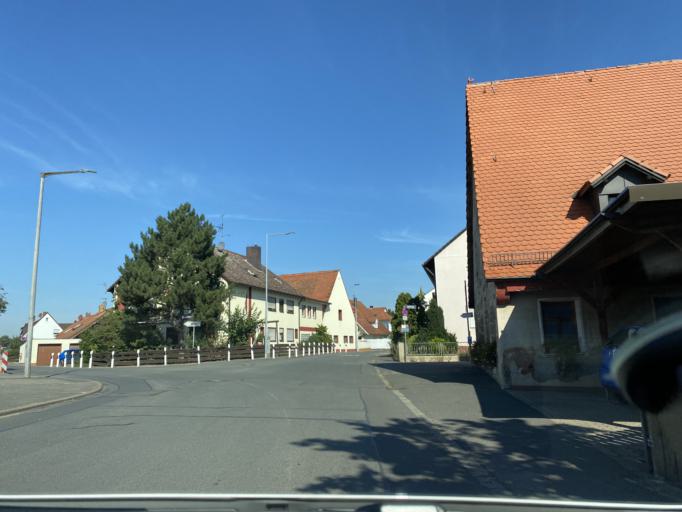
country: DE
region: Bavaria
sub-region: Regierungsbezirk Mittelfranken
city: Wetzendorf
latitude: 49.4999
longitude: 11.0194
